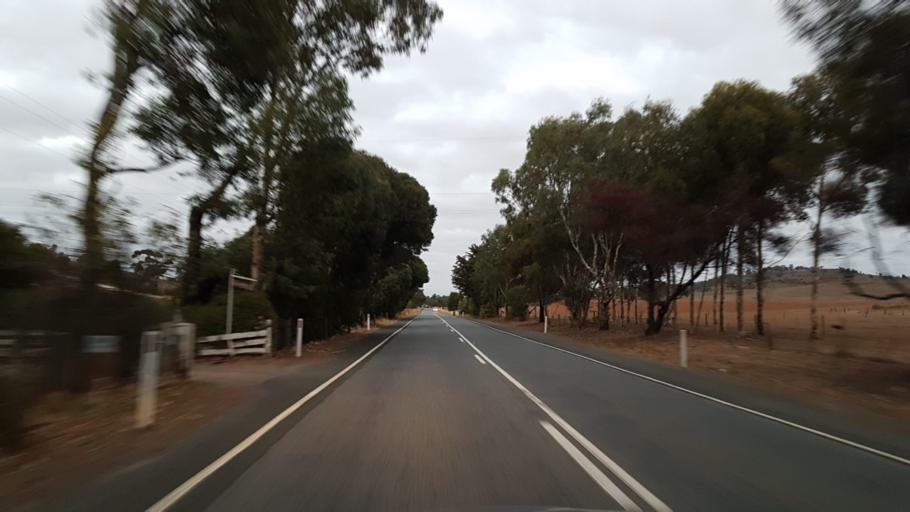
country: AU
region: South Australia
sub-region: Mount Barker
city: Callington
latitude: -35.0597
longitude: 139.0118
